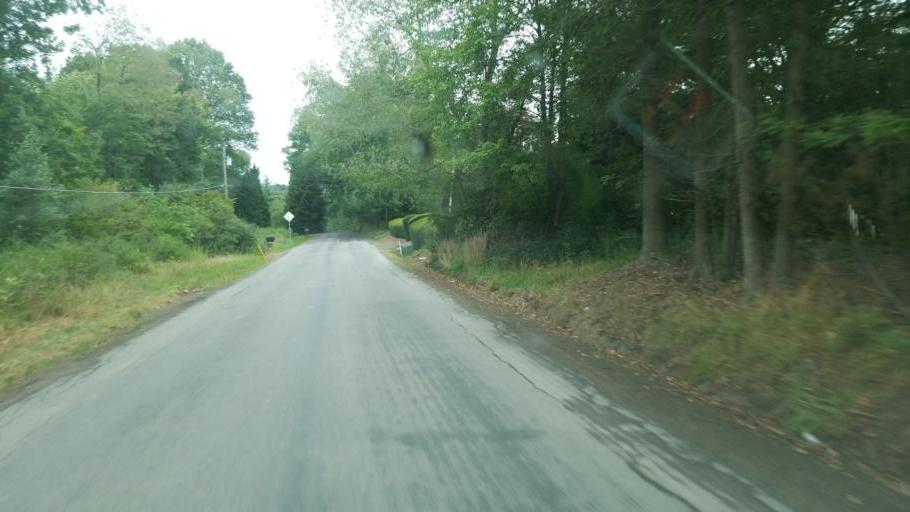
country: US
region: Pennsylvania
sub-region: Clarion County
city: Clarion
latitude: 41.1895
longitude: -79.3621
